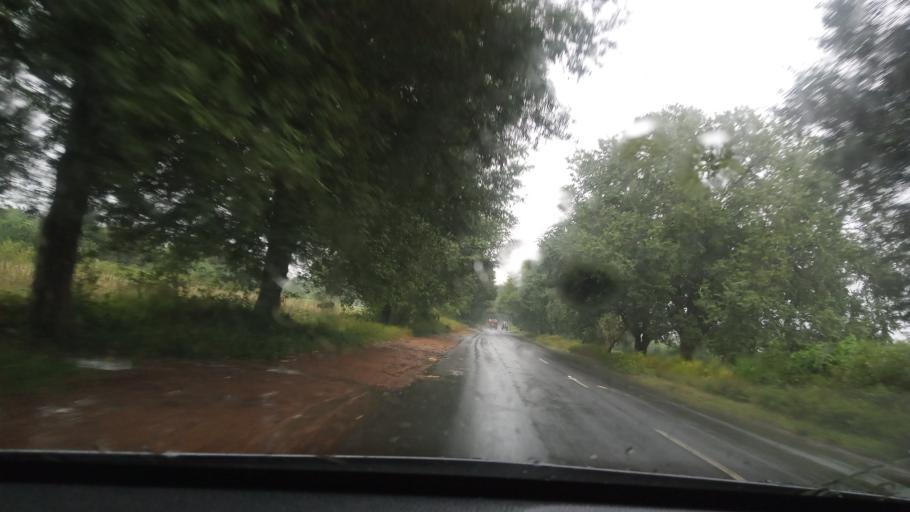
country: IN
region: Tamil Nadu
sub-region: Vellore
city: Kalavai
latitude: 12.8104
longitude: 79.4131
